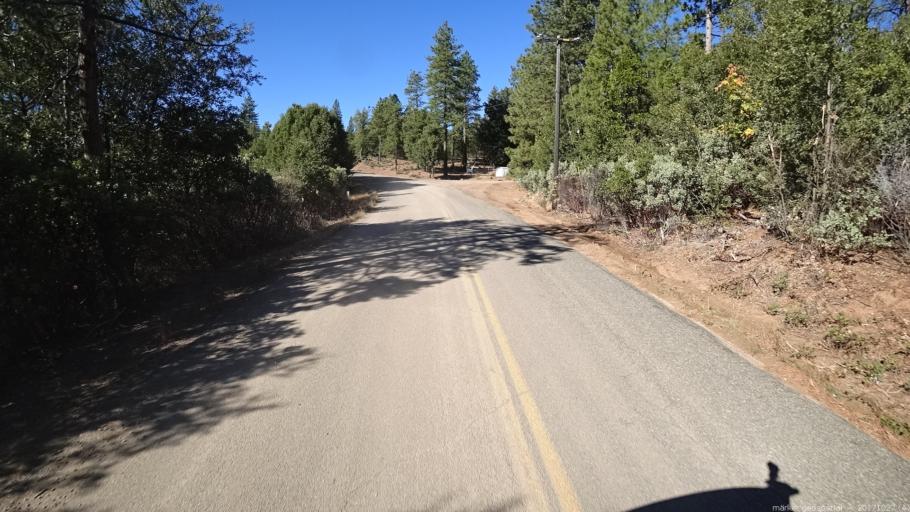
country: US
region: California
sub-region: Shasta County
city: Shingletown
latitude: 40.6616
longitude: -121.8821
